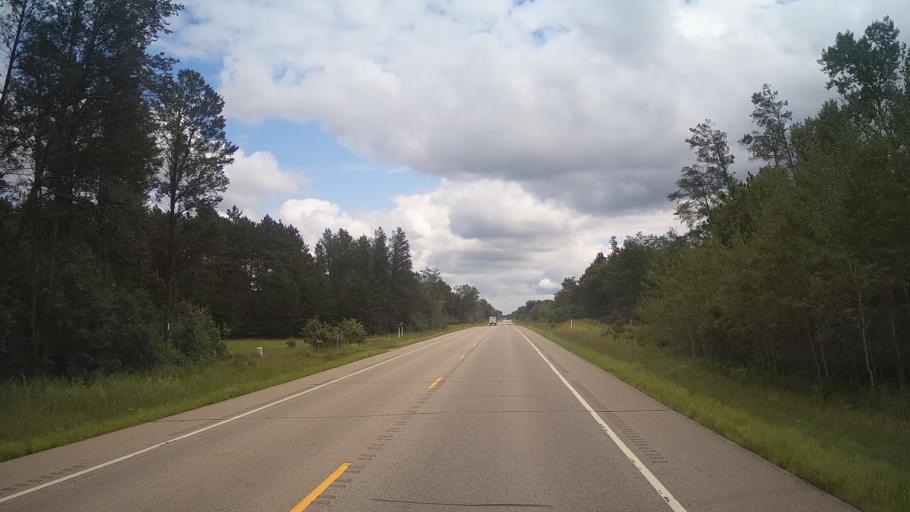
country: US
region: Wisconsin
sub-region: Adams County
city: Friendship
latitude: 44.0252
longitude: -89.7419
